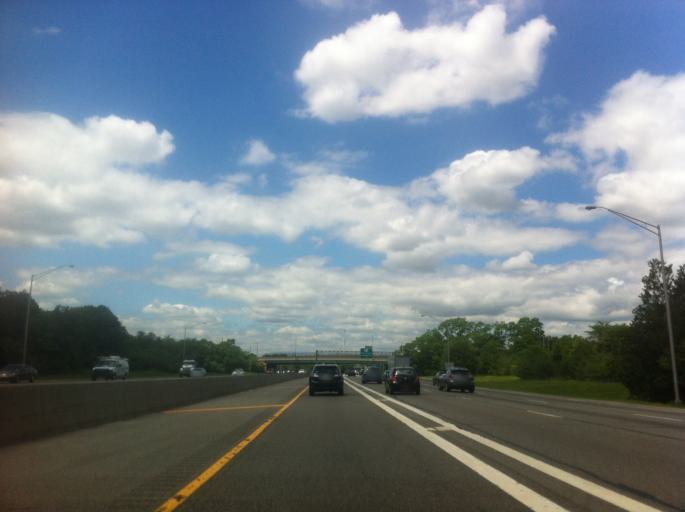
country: US
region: New York
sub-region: Suffolk County
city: Islandia
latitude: 40.8097
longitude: -73.1561
